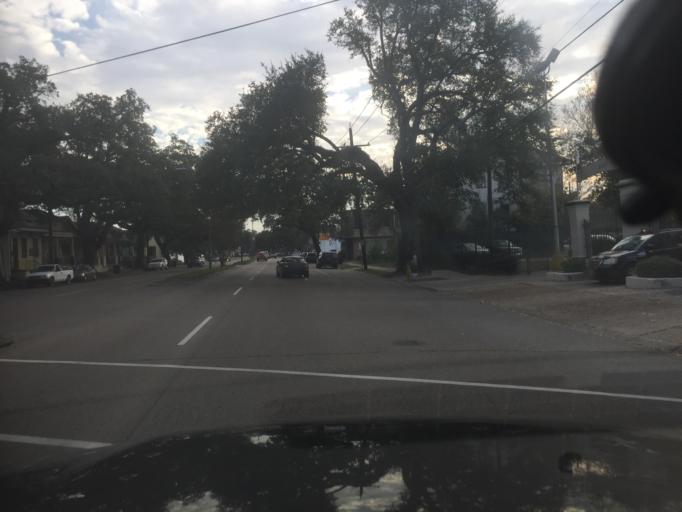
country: US
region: Louisiana
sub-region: Orleans Parish
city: New Orleans
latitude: 29.9821
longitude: -90.0772
